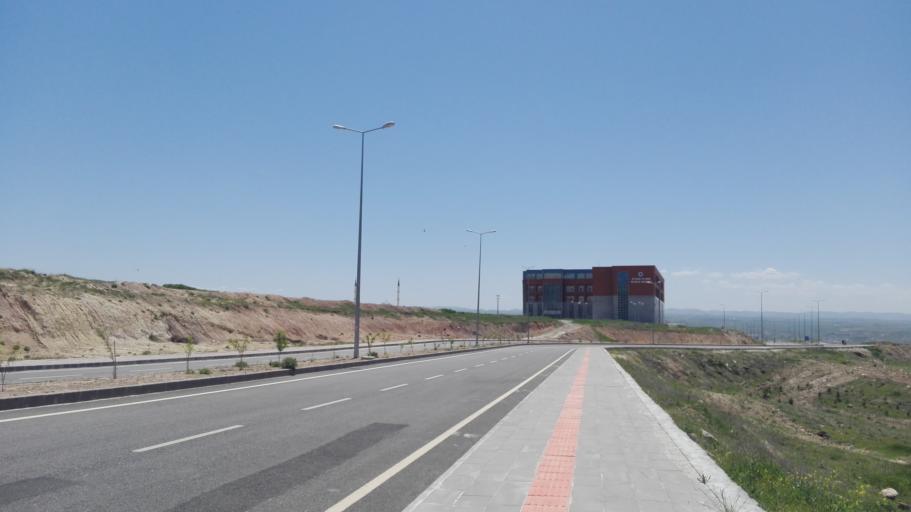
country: TR
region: Batman
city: Oymatas
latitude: 37.7921
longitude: 41.0624
